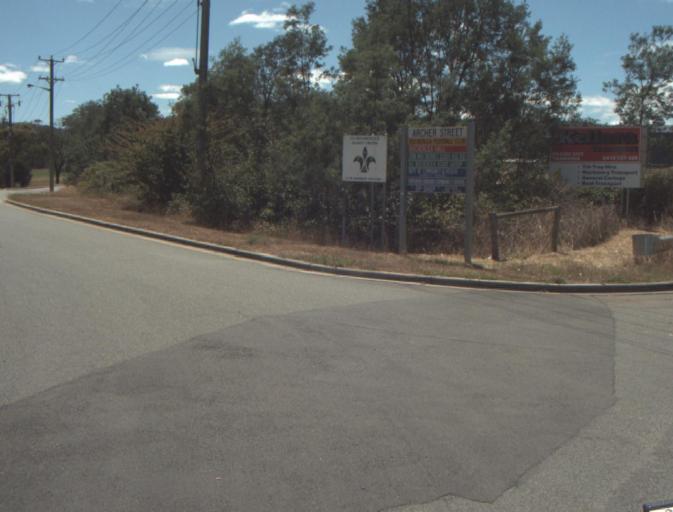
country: AU
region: Tasmania
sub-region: Launceston
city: Mayfield
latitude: -41.3766
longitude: 147.1301
